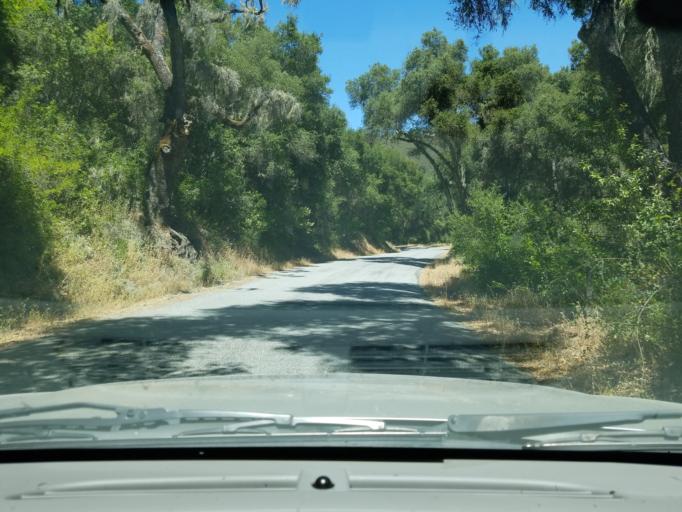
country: US
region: California
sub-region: Monterey County
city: Gonzales
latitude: 36.3761
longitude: -121.5623
